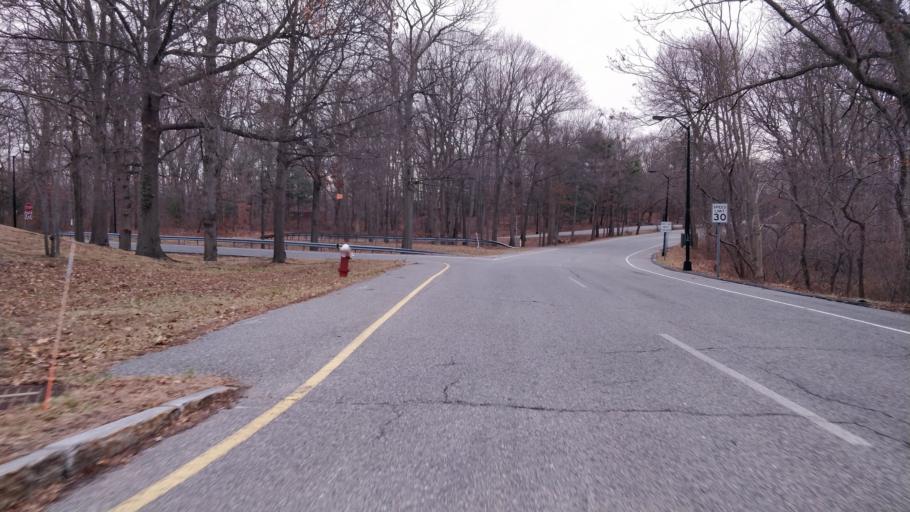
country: US
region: New York
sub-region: Nassau County
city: Brookville
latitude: 40.7997
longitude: -73.5715
